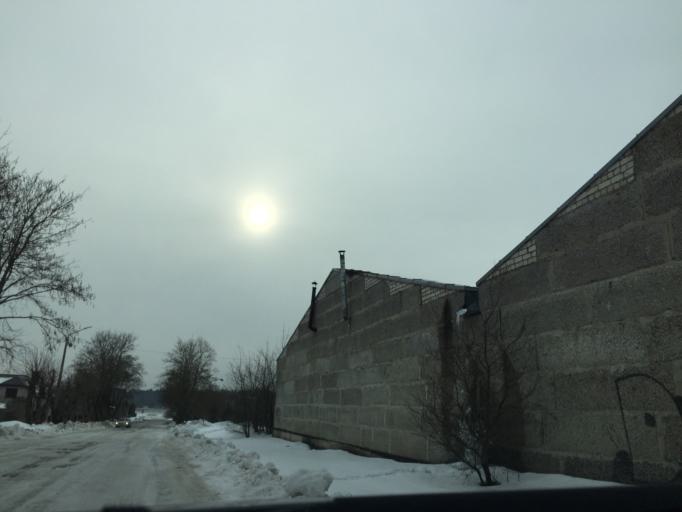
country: LV
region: Ogre
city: Ogre
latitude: 56.8214
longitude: 24.5711
